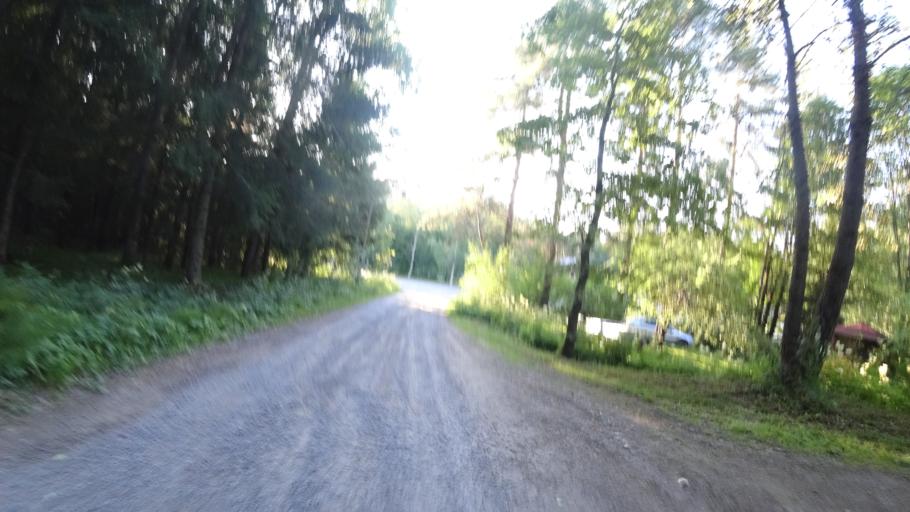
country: FI
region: Pirkanmaa
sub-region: Tampere
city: Nokia
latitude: 61.4726
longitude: 23.3771
